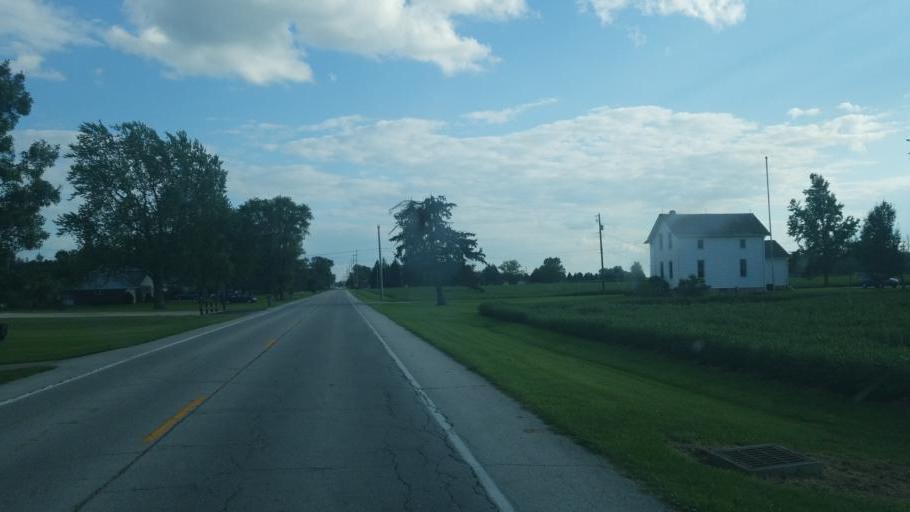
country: US
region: Ohio
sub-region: Sandusky County
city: Ballville
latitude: 41.3164
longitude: -83.1299
